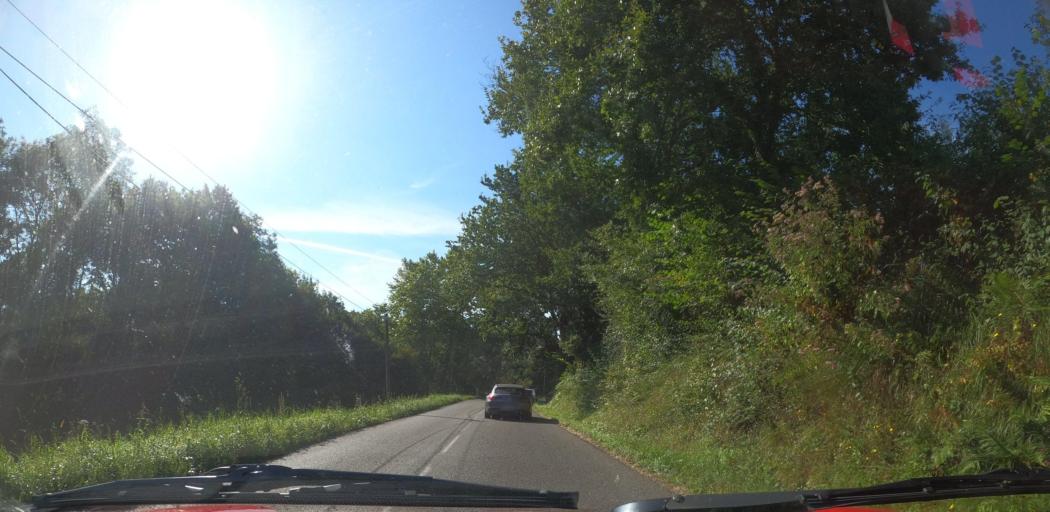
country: FR
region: Aquitaine
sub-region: Departement des Pyrenees-Atlantiques
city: Saint-Pee-sur-Nivelle
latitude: 43.3680
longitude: -1.5451
